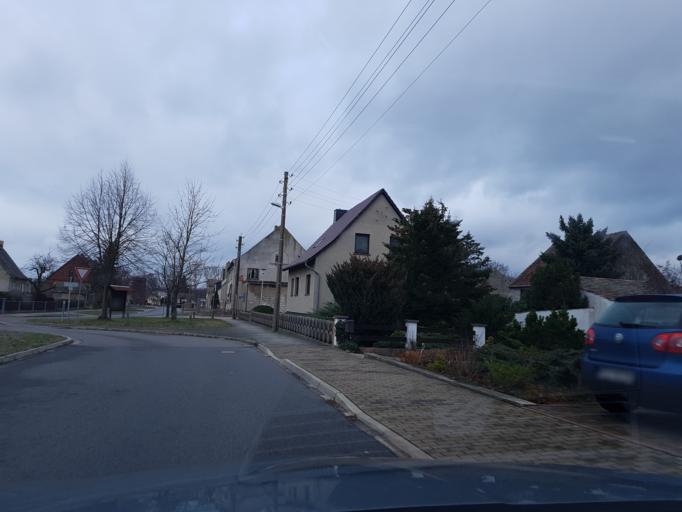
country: DE
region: Brandenburg
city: Bad Liebenwerda
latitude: 51.4793
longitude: 13.4249
